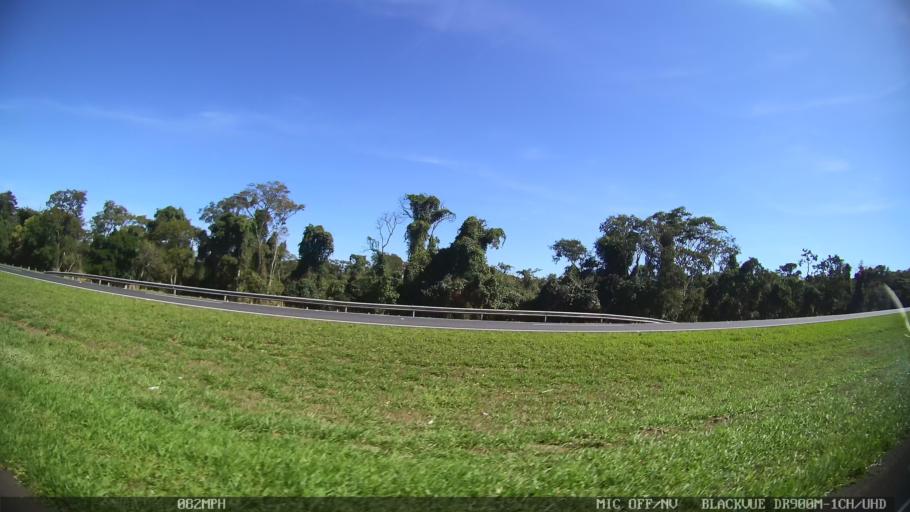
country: BR
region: Sao Paulo
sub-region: Sao Simao
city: Sao Simao
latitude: -21.6259
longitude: -47.6145
